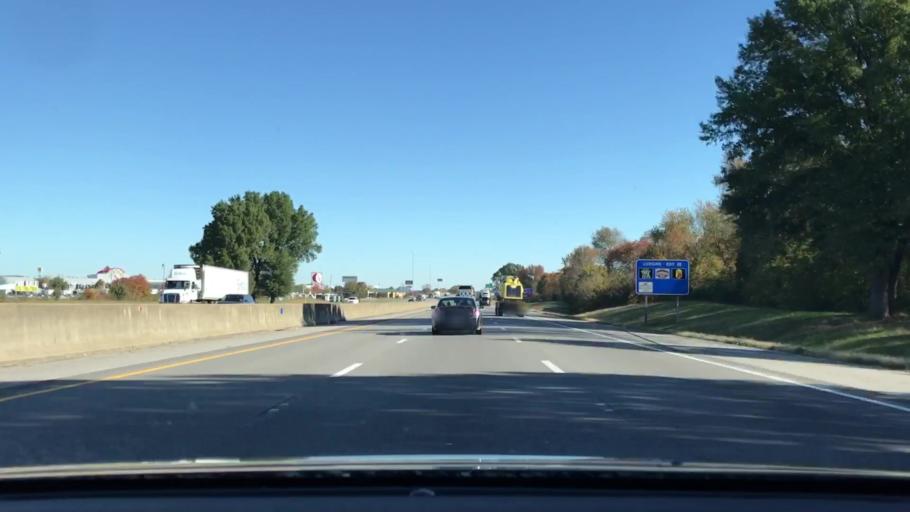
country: US
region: Kentucky
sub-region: Warren County
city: Bowling Green
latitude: 36.9993
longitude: -86.3762
